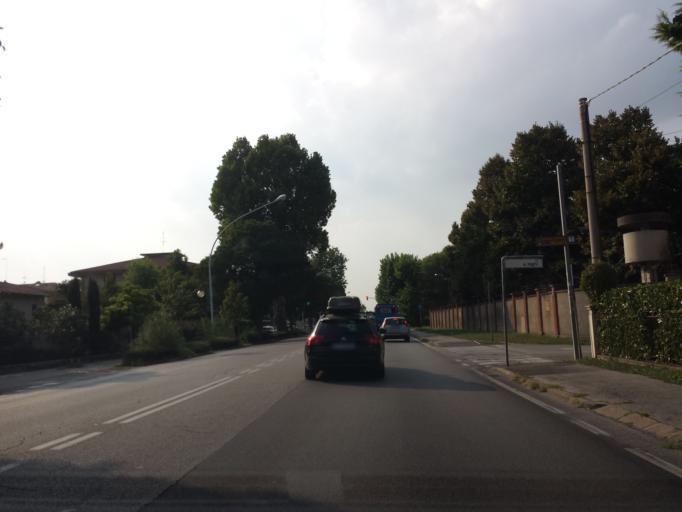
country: IT
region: Veneto
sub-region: Provincia di Padova
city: Caselle
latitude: 45.4120
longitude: 11.8422
